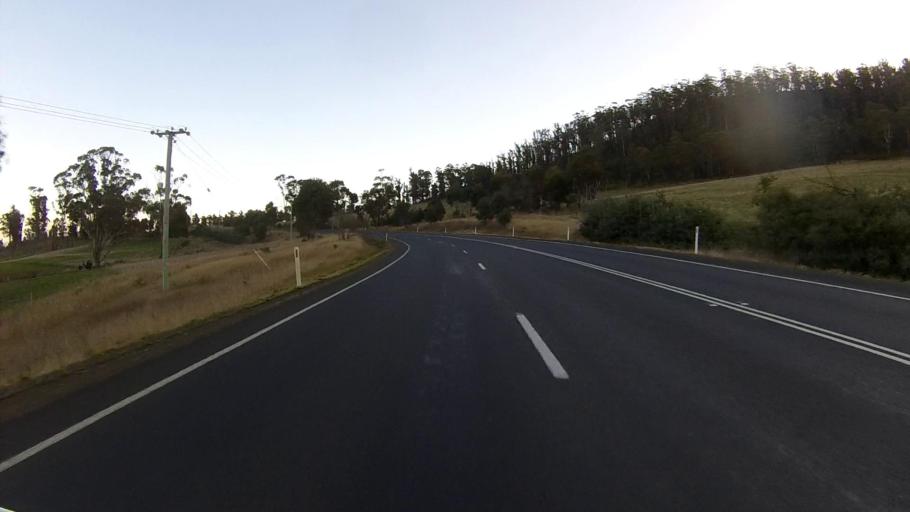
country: AU
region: Tasmania
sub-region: Sorell
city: Sorell
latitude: -42.8207
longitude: 147.7432
